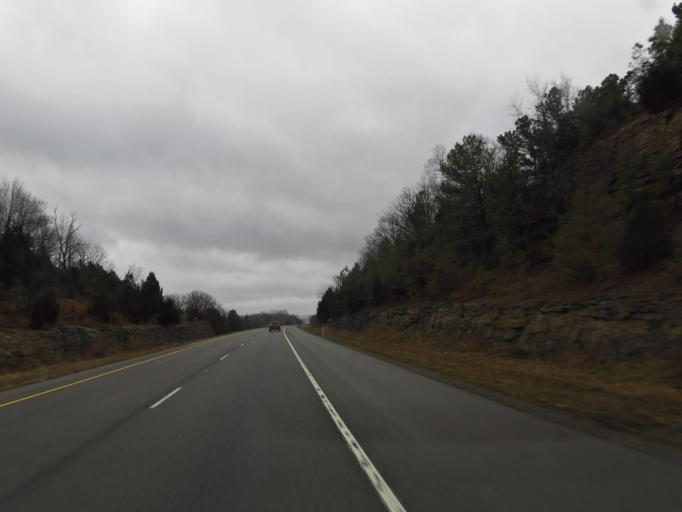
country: US
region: Illinois
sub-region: Johnson County
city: Vienna
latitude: 37.4952
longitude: -88.8969
